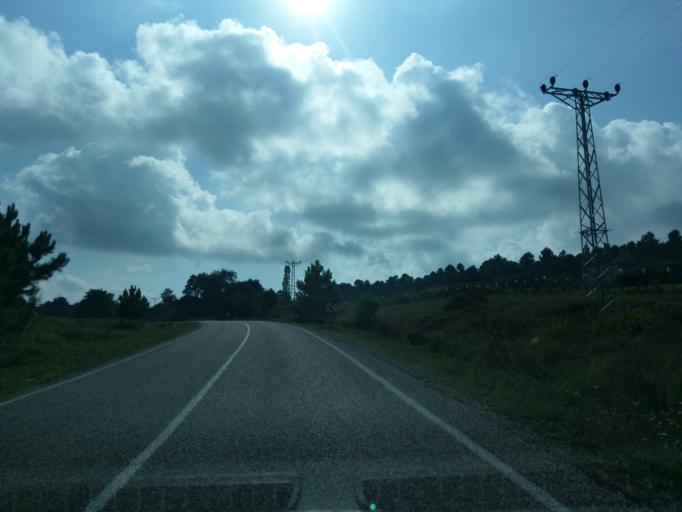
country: TR
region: Sinop
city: Erfelek
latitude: 41.9949
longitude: 34.8900
